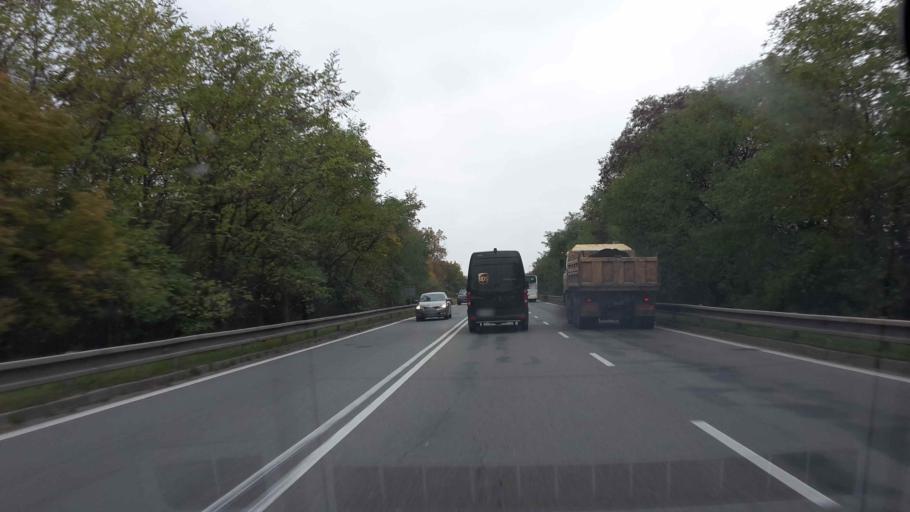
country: CZ
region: South Moravian
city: Slavkov u Brna
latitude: 49.1592
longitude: 16.8576
